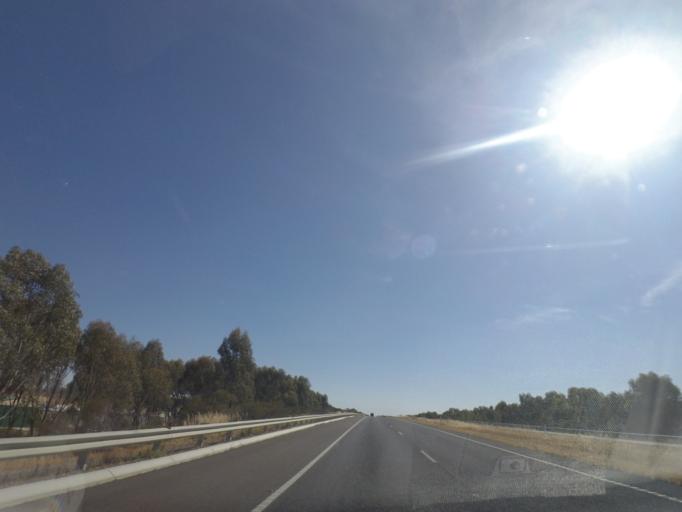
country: AU
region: Victoria
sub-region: Greater Shepparton
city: Shepparton
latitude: -36.6783
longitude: 145.2425
